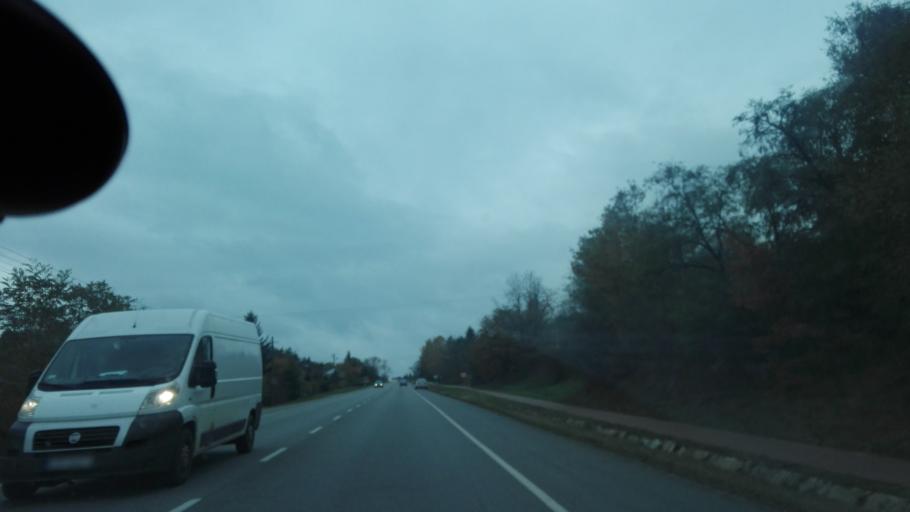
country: PL
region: Lublin Voivodeship
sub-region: Powiat pulawski
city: Pulawy
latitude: 51.4098
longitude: 21.9281
